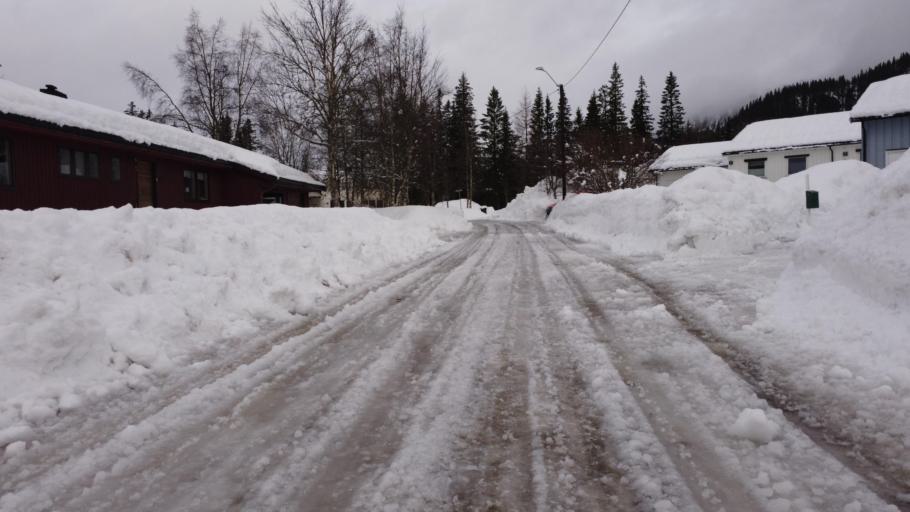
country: NO
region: Nordland
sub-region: Rana
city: Mo i Rana
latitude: 66.3343
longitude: 14.1507
